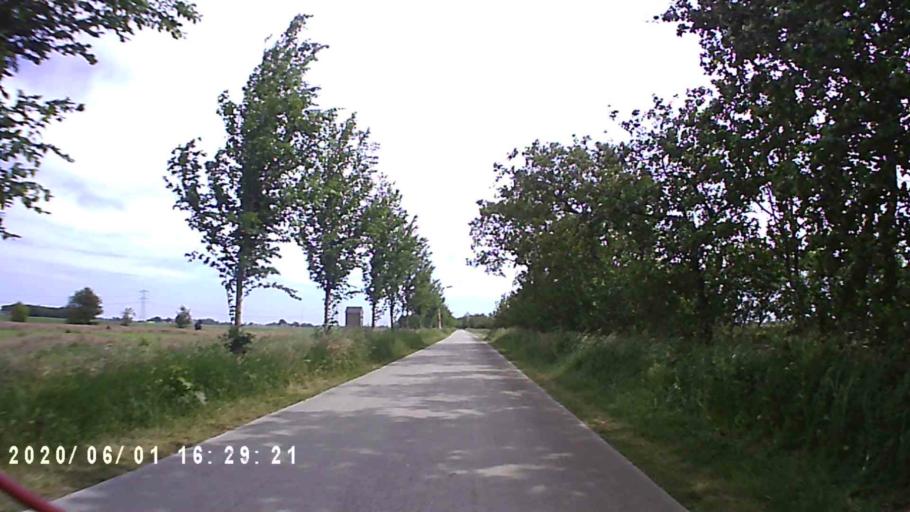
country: NL
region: Friesland
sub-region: Gemeente Leeuwarden
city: Camminghaburen
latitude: 53.1864
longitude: 5.8661
